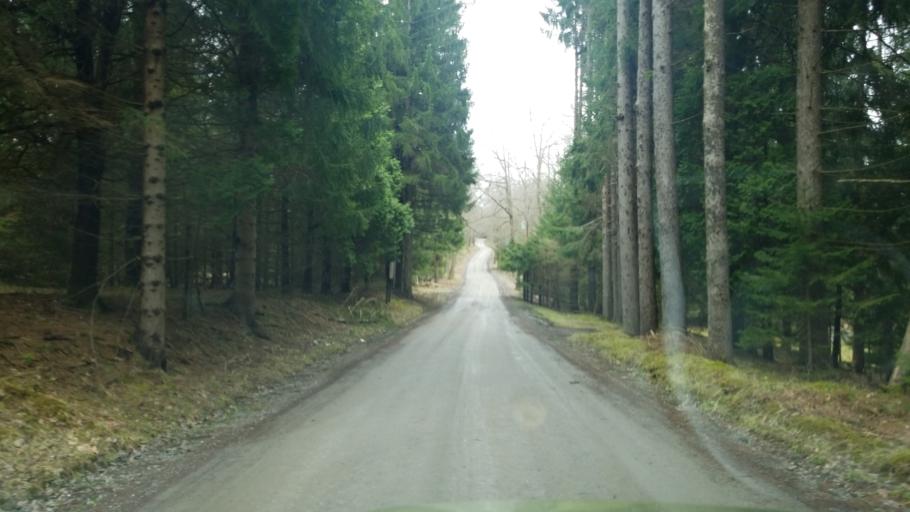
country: US
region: Pennsylvania
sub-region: Clearfield County
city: Shiloh
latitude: 41.1705
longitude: -78.2844
